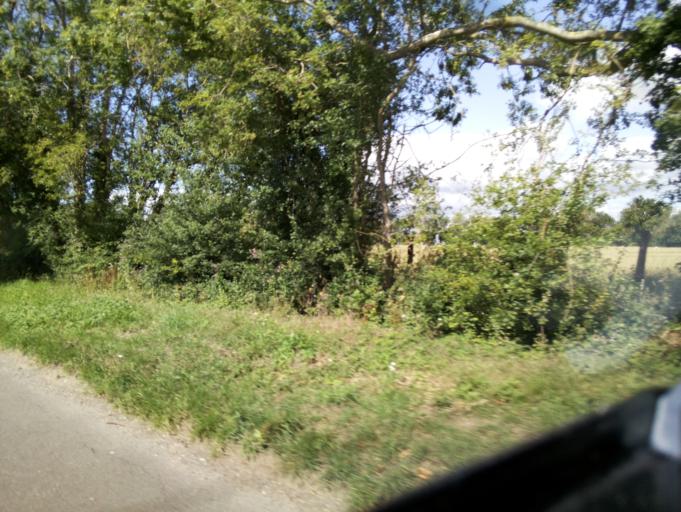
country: GB
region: England
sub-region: Buckinghamshire
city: Buckingham
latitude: 51.9939
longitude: -0.9260
